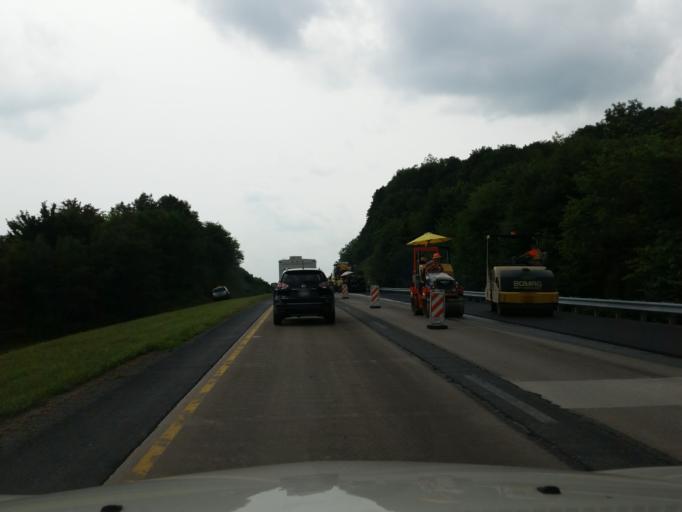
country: US
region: Pennsylvania
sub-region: Juniata County
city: Mifflintown
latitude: 40.5631
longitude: -77.2637
